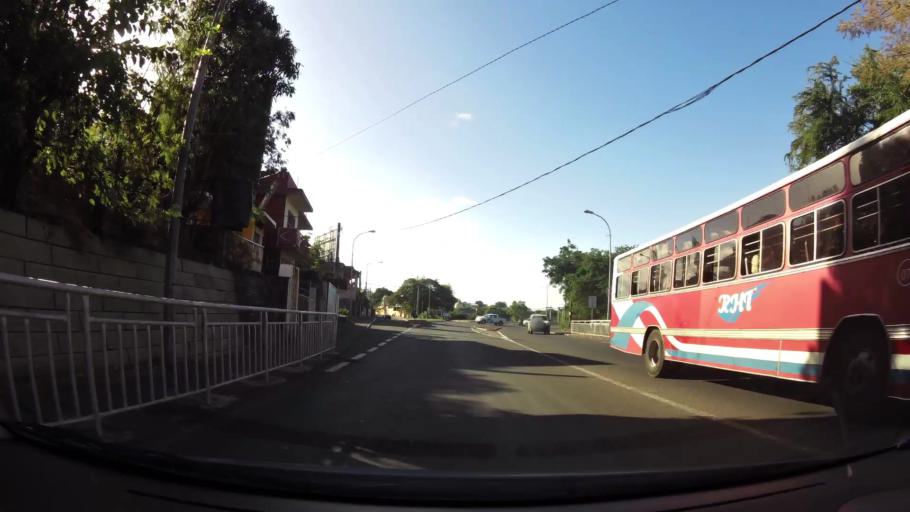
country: MU
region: Moka
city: Pailles
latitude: -20.1764
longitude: 57.4711
